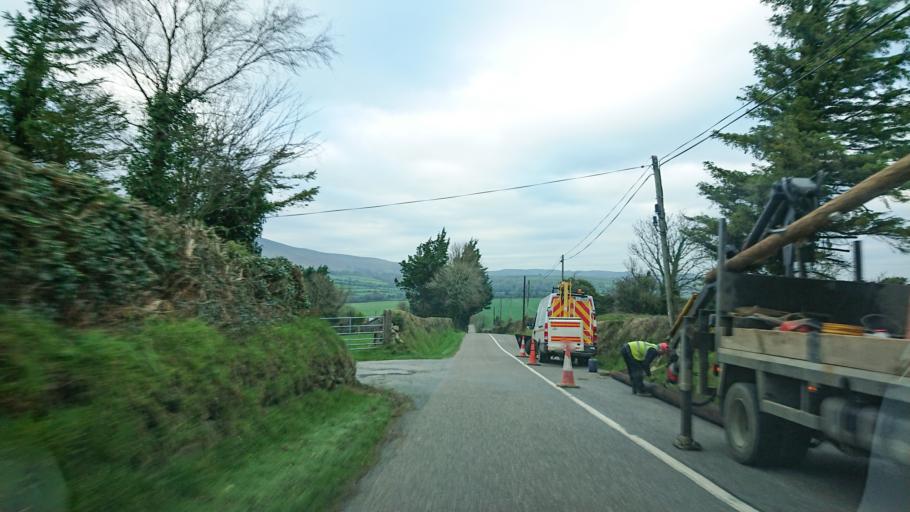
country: IE
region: Munster
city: Carrick-on-Suir
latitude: 52.3130
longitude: -7.5272
